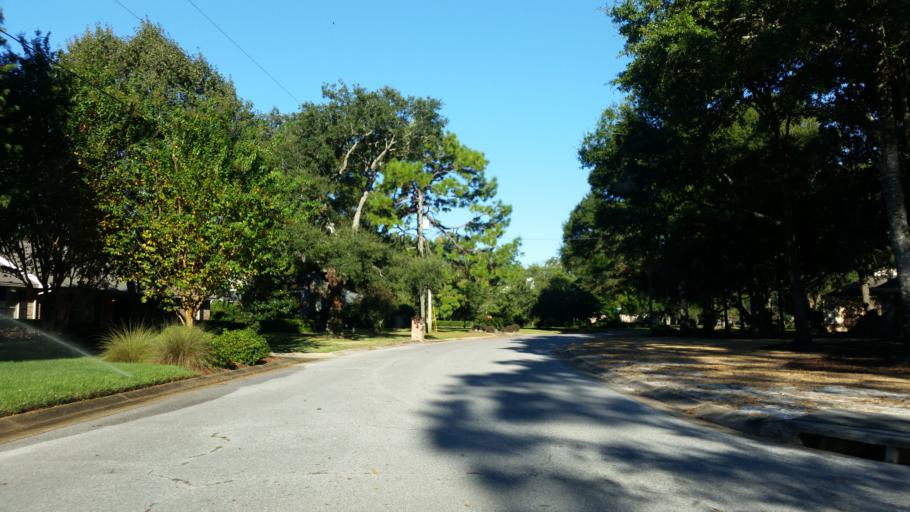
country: US
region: Florida
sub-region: Escambia County
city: East Pensacola Heights
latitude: 30.4692
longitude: -87.1686
